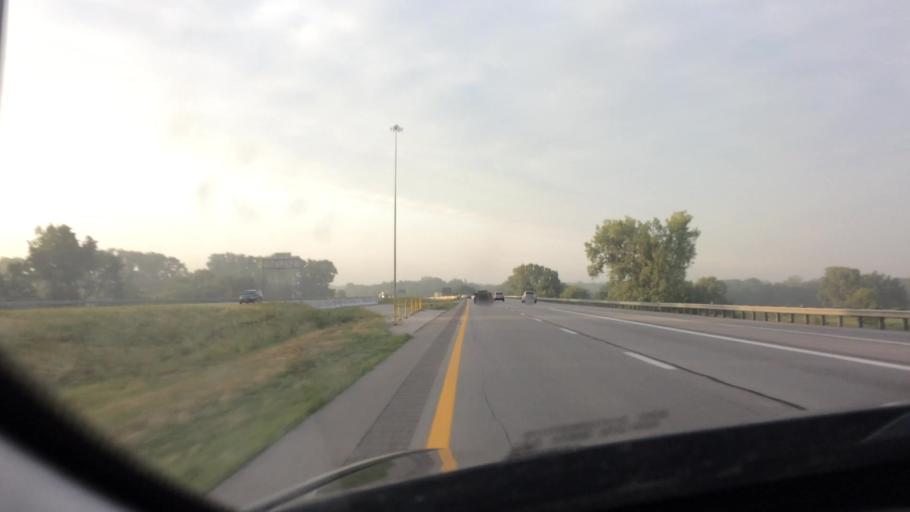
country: US
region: Ohio
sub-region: Lucas County
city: Maumee
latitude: 41.5494
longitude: -83.6846
